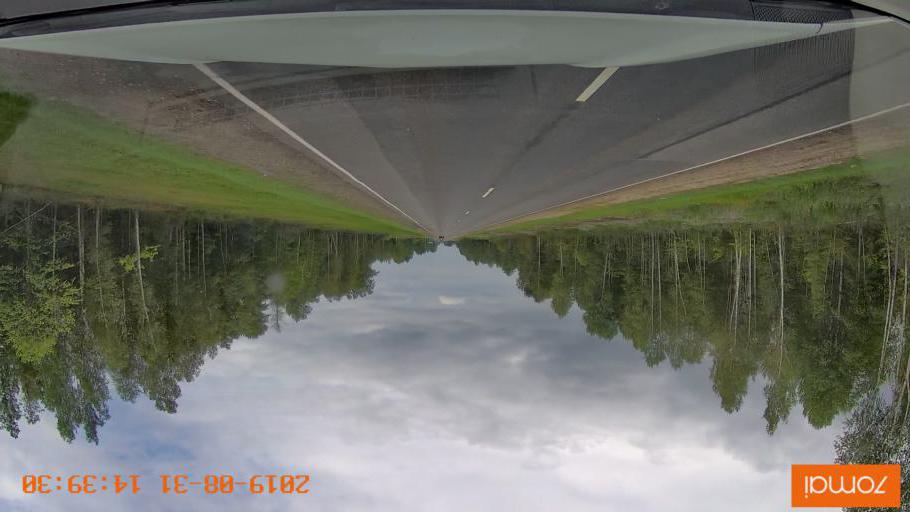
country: RU
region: Smolensk
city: Yekimovichi
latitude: 54.1921
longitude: 33.5542
